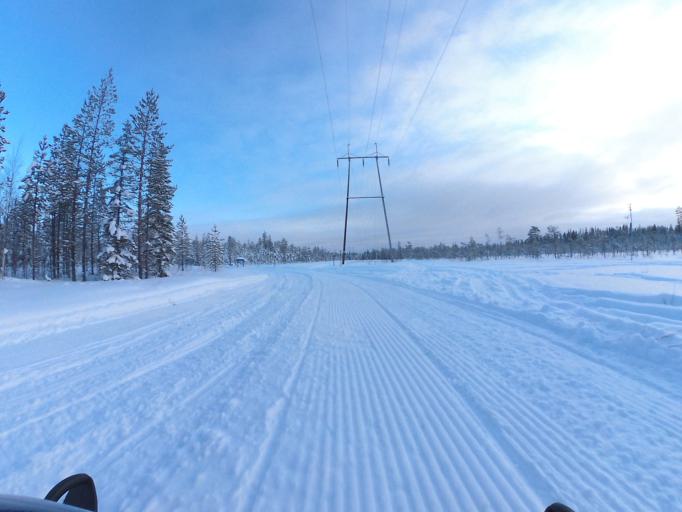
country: FI
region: Lapland
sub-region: Rovaniemi
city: Rovaniemi
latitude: 66.5118
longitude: 25.9593
